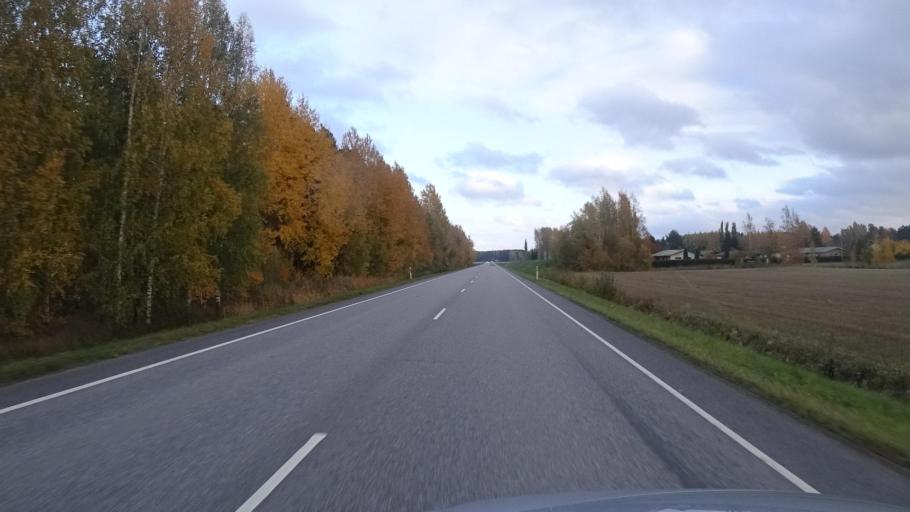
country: FI
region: Satakunta
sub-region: Rauma
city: Saekylae
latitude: 61.0437
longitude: 22.3695
